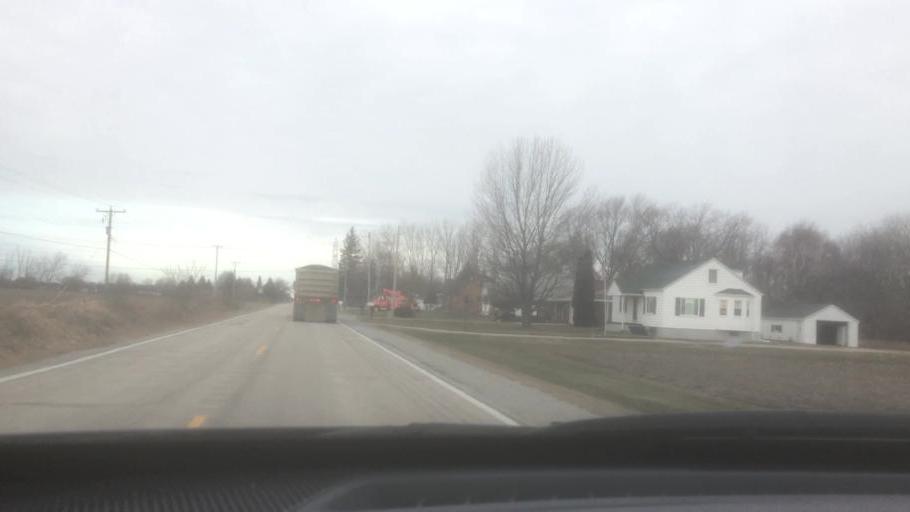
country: US
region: Michigan
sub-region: Bay County
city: Essexville
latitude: 43.5221
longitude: -83.7874
